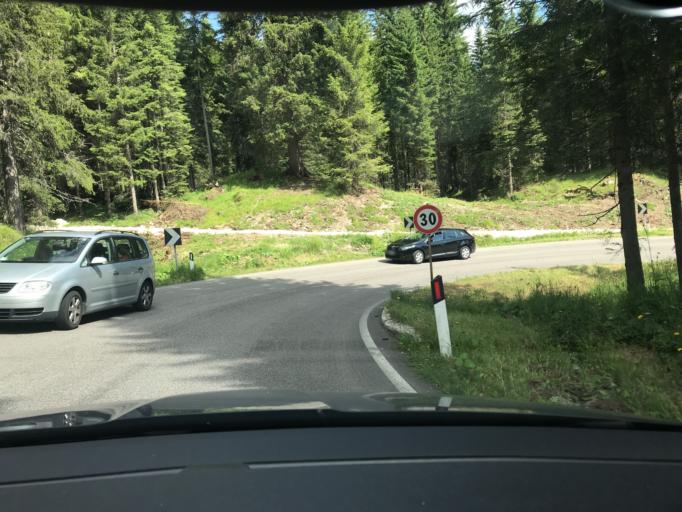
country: IT
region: Veneto
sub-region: Provincia di Belluno
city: Cortina d'Ampezzo
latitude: 46.5211
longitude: 12.0955
